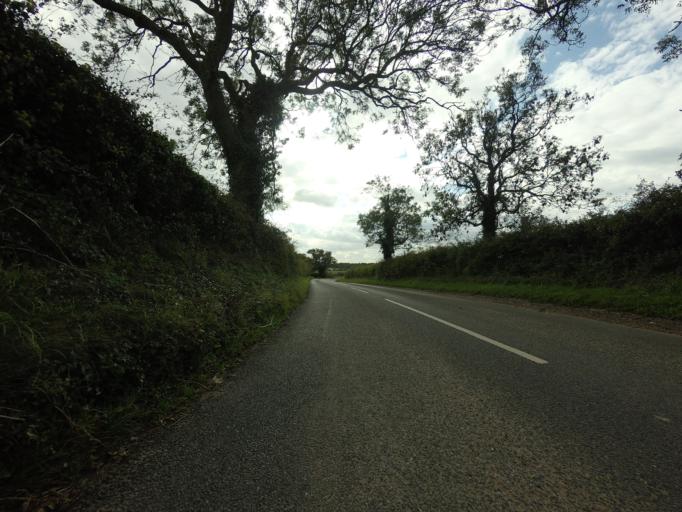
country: GB
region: England
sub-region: Norfolk
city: Snettisham
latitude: 52.8800
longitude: 0.5172
